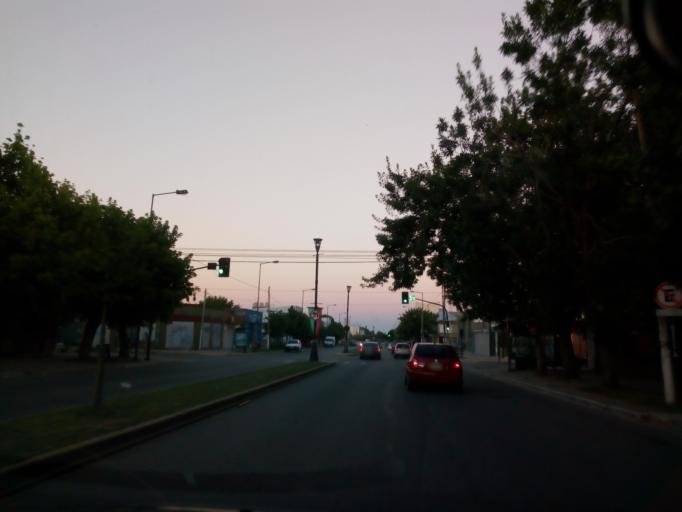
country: AR
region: Buenos Aires
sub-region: Partido de La Plata
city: La Plata
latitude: -34.9276
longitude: -57.9984
